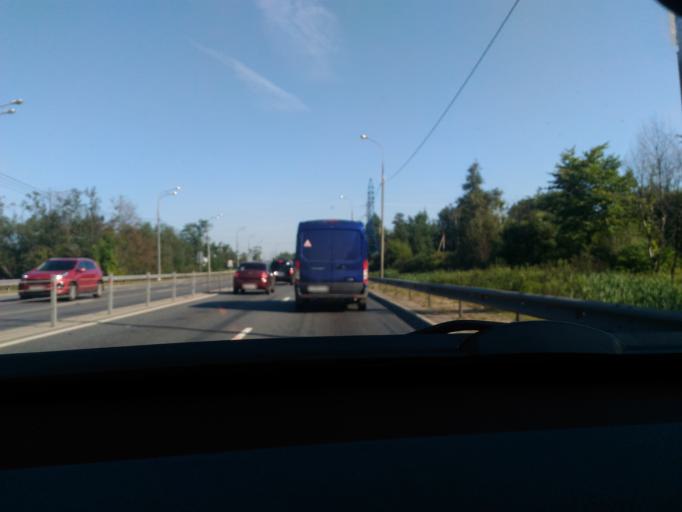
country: RU
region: Moskovskaya
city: Podosinki
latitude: 56.2005
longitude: 37.5243
